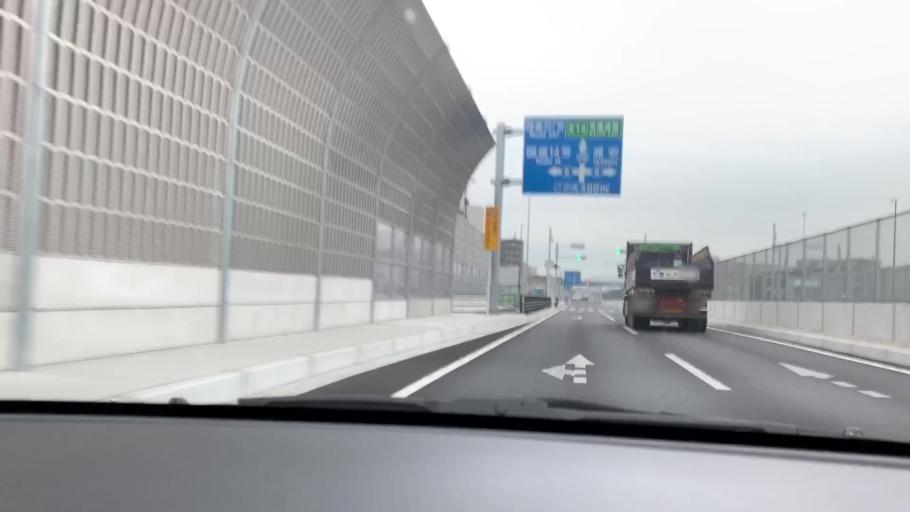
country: JP
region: Tokyo
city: Urayasu
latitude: 35.7175
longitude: 139.9185
